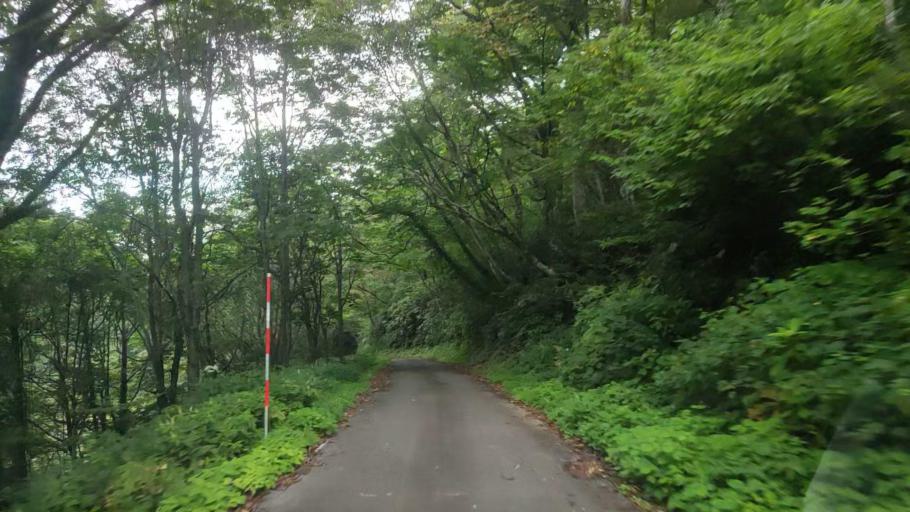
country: JP
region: Toyama
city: Yatsuomachi-higashikumisaka
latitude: 36.3992
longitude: 137.0742
